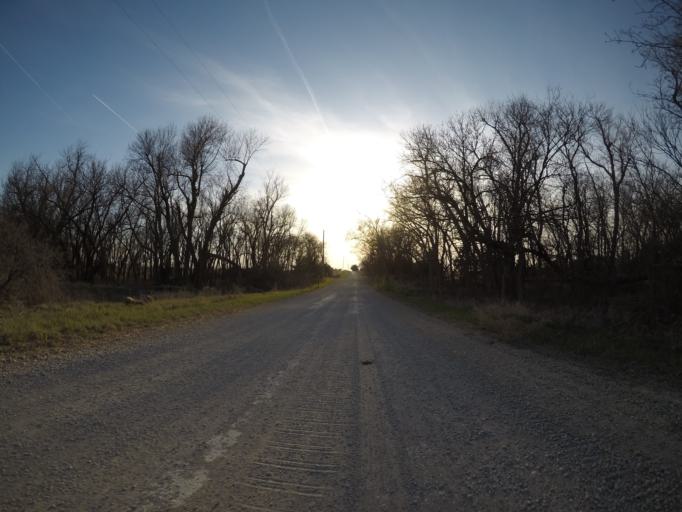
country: US
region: Kansas
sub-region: Riley County
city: Manhattan
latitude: 39.2545
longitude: -96.6767
